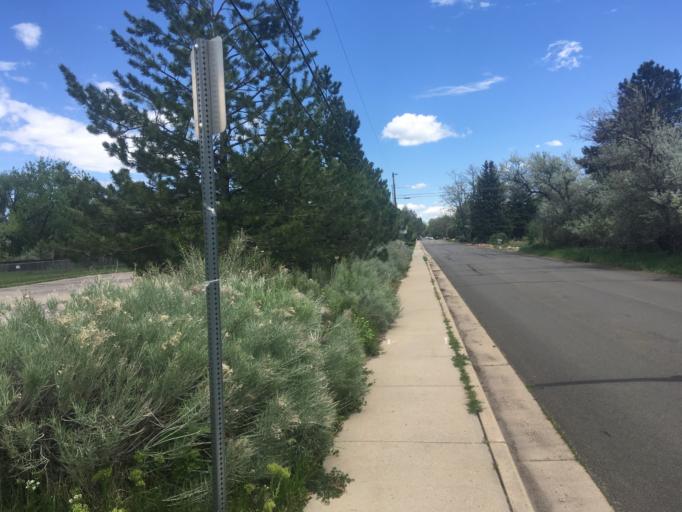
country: US
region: Colorado
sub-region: Boulder County
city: Boulder
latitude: 40.0065
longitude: -105.2323
